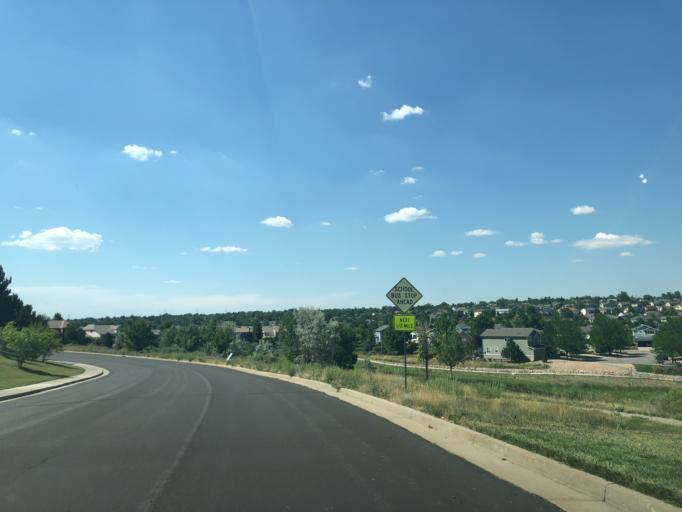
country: US
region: Colorado
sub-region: Arapahoe County
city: Dove Valley
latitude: 39.6053
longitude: -104.7793
